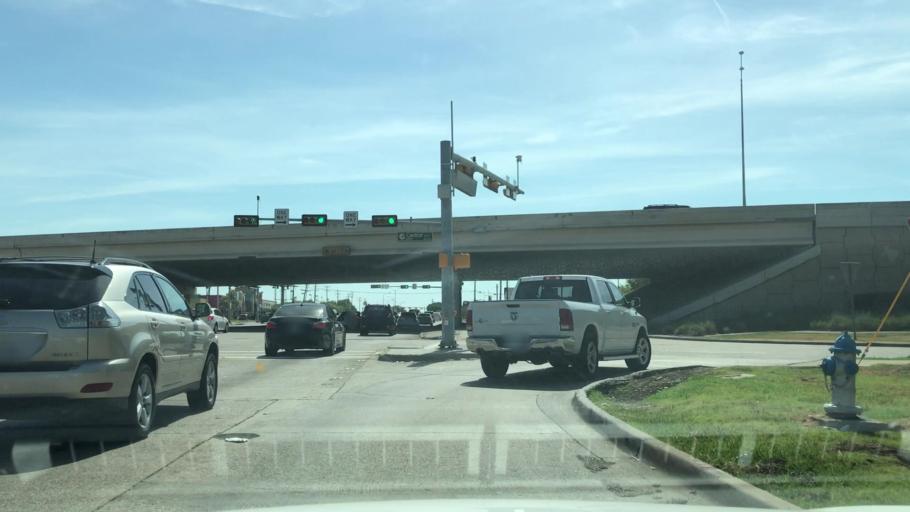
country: US
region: Texas
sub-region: Collin County
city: Plano
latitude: 33.0572
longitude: -96.6949
